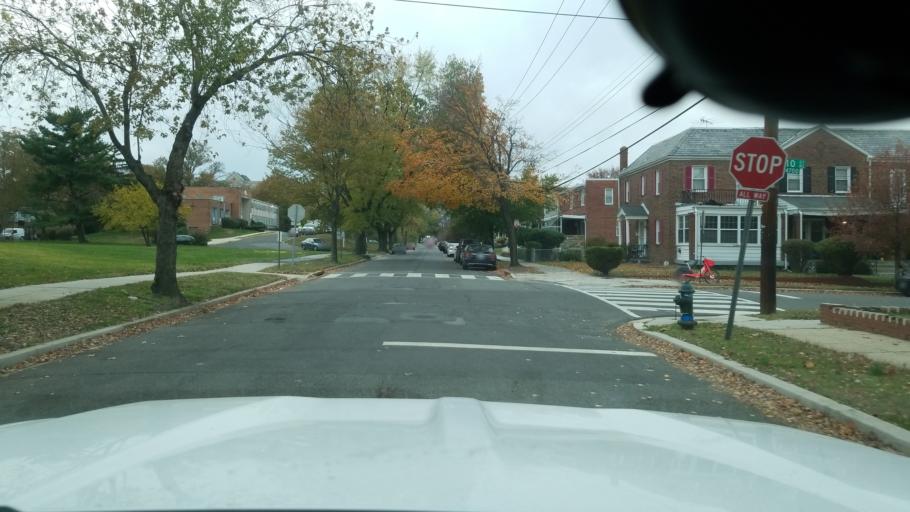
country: US
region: Maryland
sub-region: Prince George's County
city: Chillum
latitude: 38.9463
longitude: -76.9925
